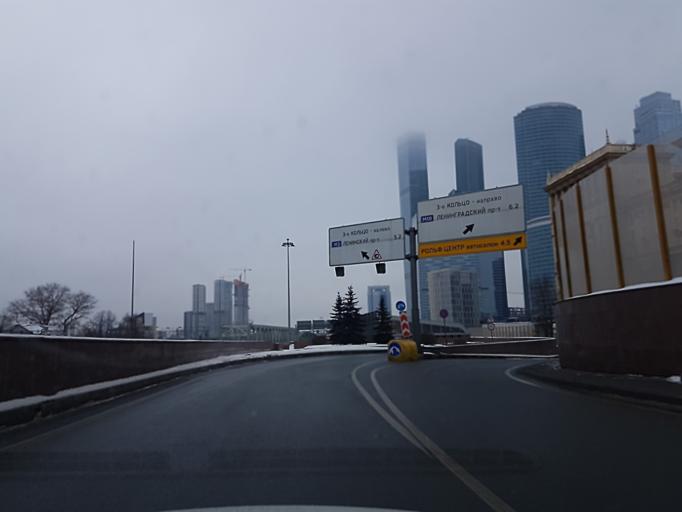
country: RU
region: Moskovskaya
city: Presnenskiy
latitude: 55.7414
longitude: 37.5344
